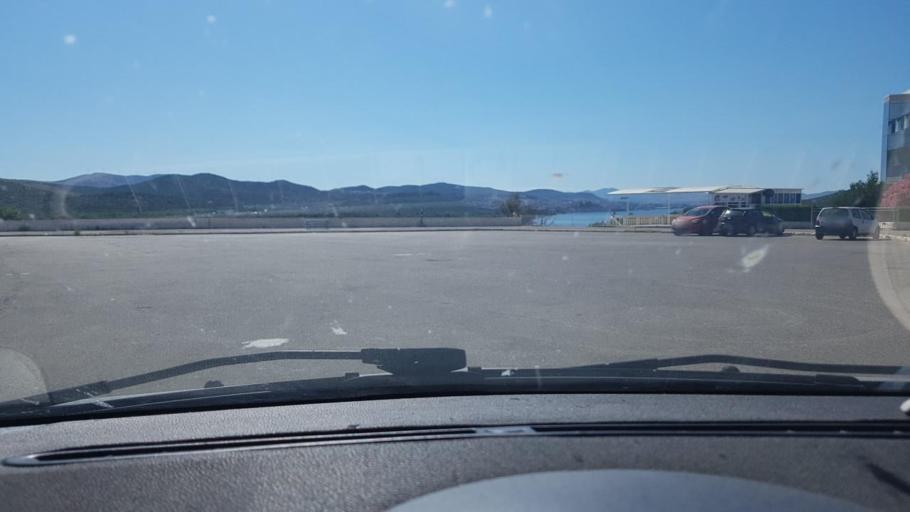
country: HR
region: Sibensko-Kniniska
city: Zaton
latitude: 43.7625
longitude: 15.8458
